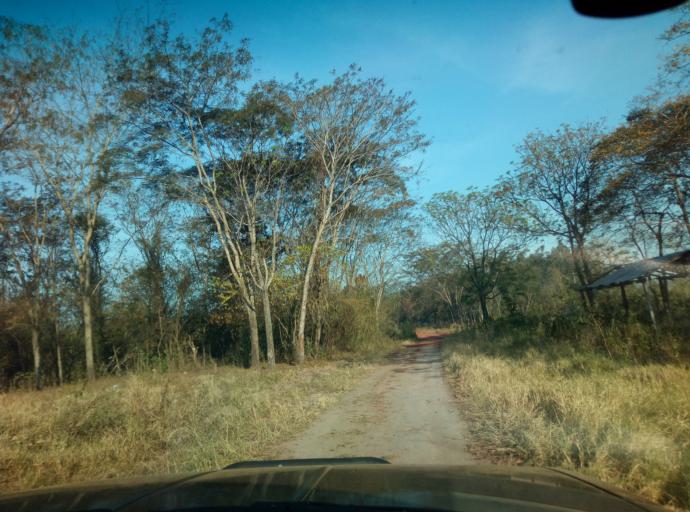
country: PY
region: Caaguazu
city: Doctor Cecilio Baez
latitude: -25.1988
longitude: -56.1368
